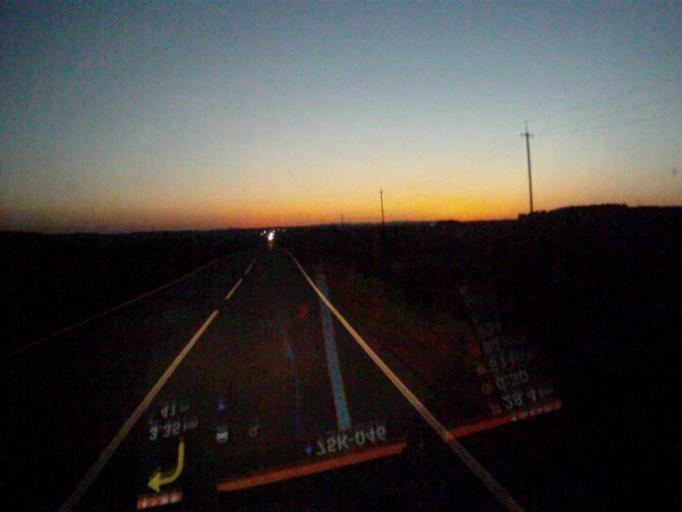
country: RU
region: Chelyabinsk
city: Chebarkul'
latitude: 55.2209
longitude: 60.5014
